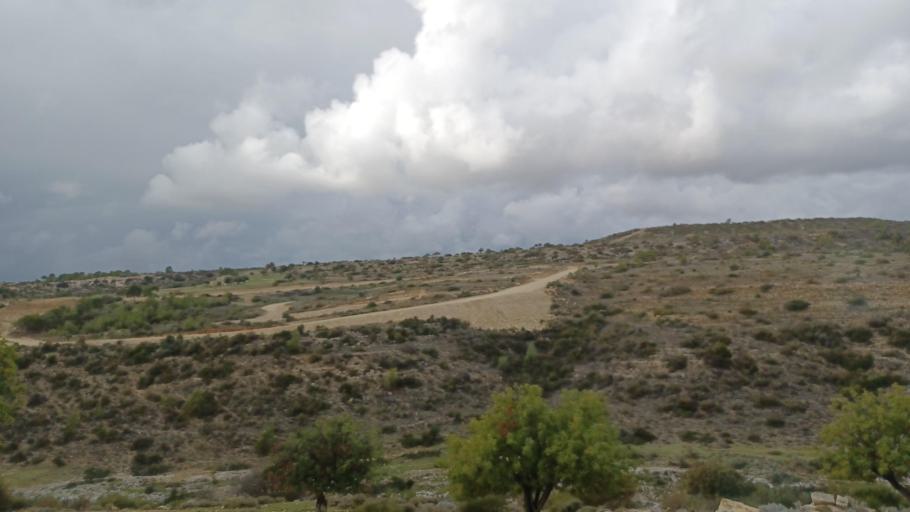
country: CY
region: Limassol
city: Sotira
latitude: 34.7292
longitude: 32.8210
